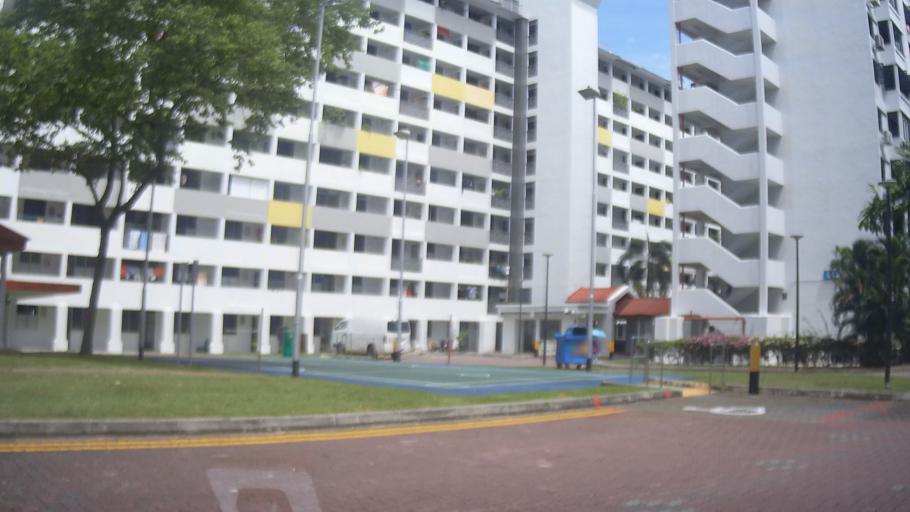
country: SG
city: Singapore
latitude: 1.3249
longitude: 103.8870
